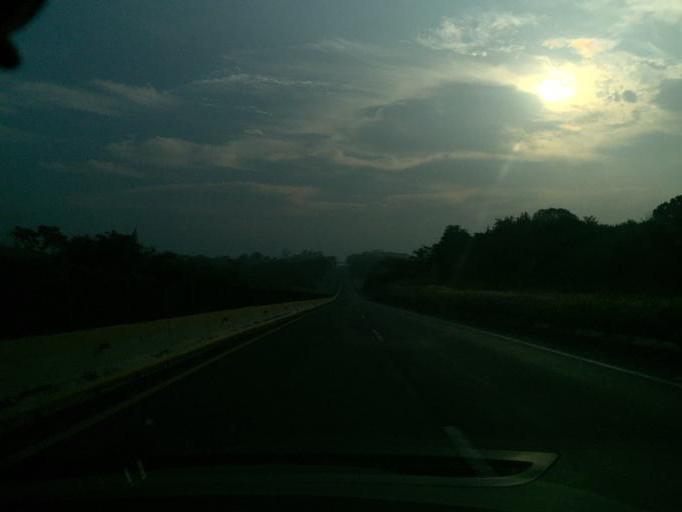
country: MX
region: Veracruz
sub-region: Omealca
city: Mata Tenatito (Casco Hacienda)
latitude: 18.7880
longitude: -96.5557
